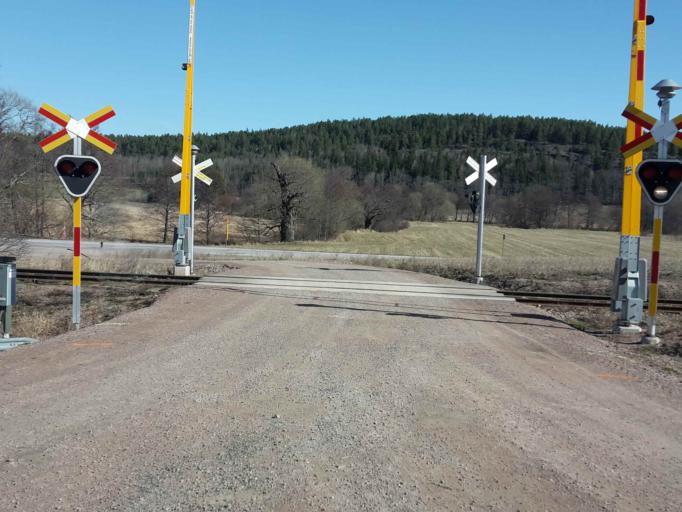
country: SE
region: Kalmar
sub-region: Vasterviks Kommun
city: Overum
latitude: 58.1350
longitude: 16.2202
